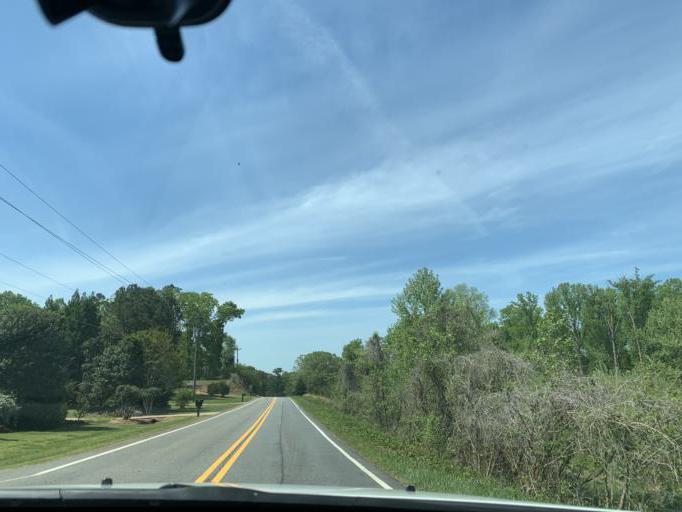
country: US
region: Georgia
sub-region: Forsyth County
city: Cumming
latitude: 34.2746
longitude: -84.2110
